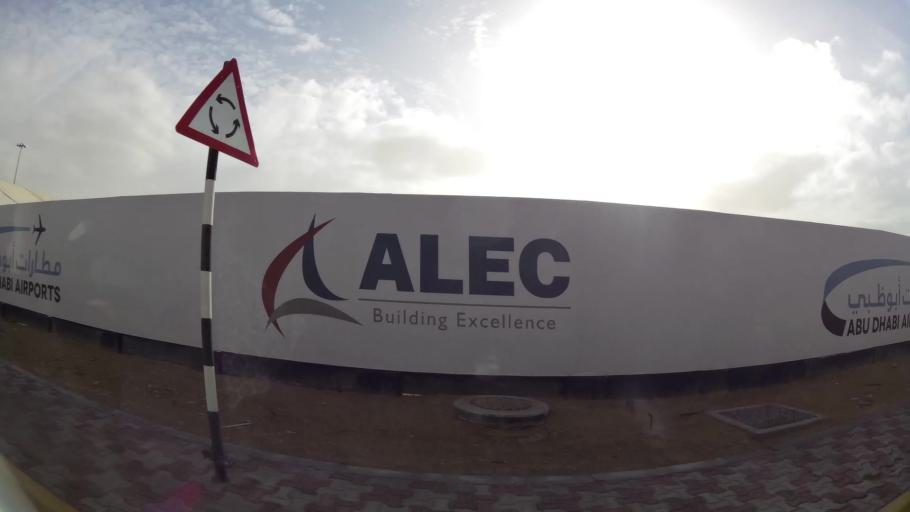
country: AE
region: Abu Dhabi
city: Abu Dhabi
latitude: 24.4271
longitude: 54.6424
